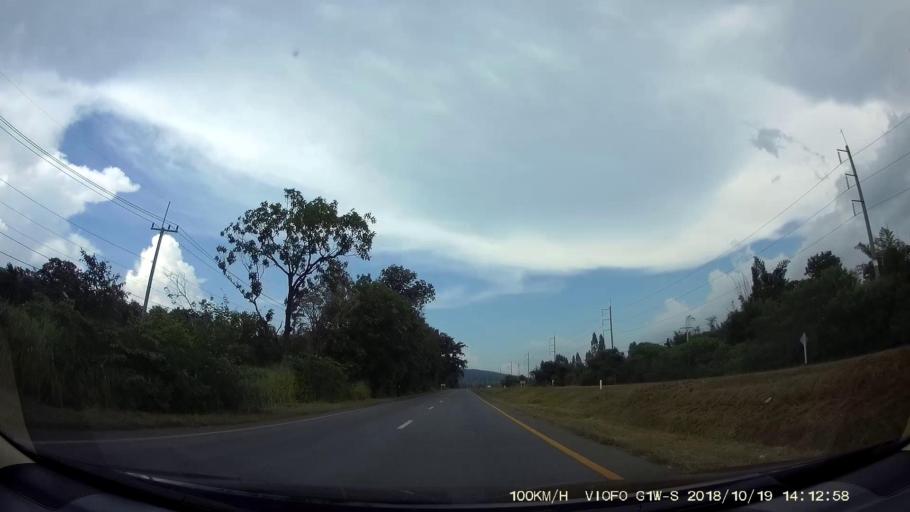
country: TH
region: Chaiyaphum
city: Khon Sawan
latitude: 15.9549
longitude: 102.1779
